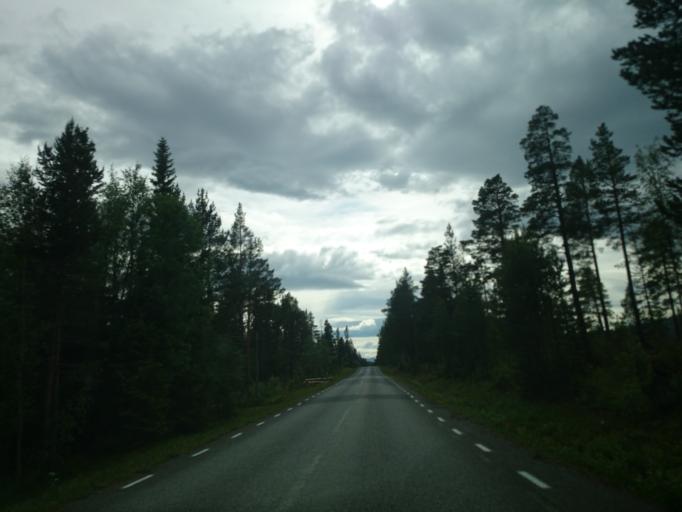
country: SE
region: Jaemtland
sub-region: Are Kommun
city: Are
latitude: 63.1822
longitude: 13.1167
